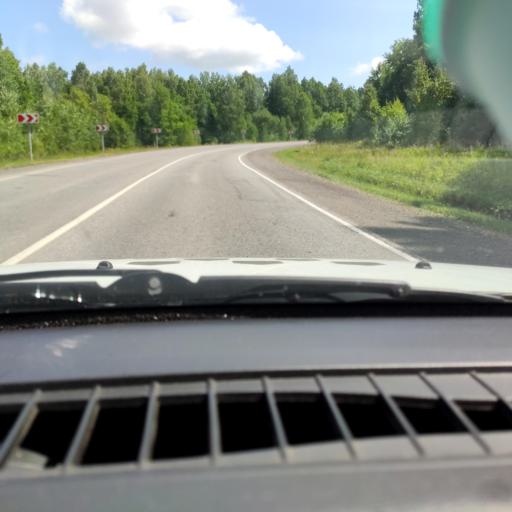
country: RU
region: Bashkortostan
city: Verkhniye Kigi
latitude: 55.3849
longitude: 58.6738
